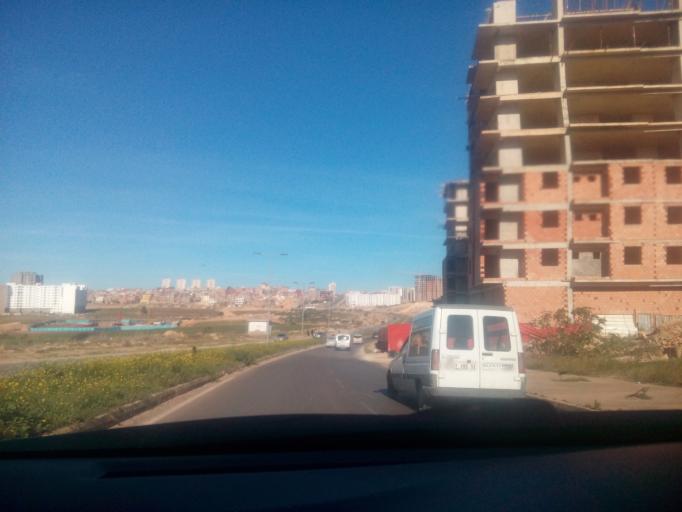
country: DZ
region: Oran
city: Bir el Djir
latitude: 35.7365
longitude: -0.5455
